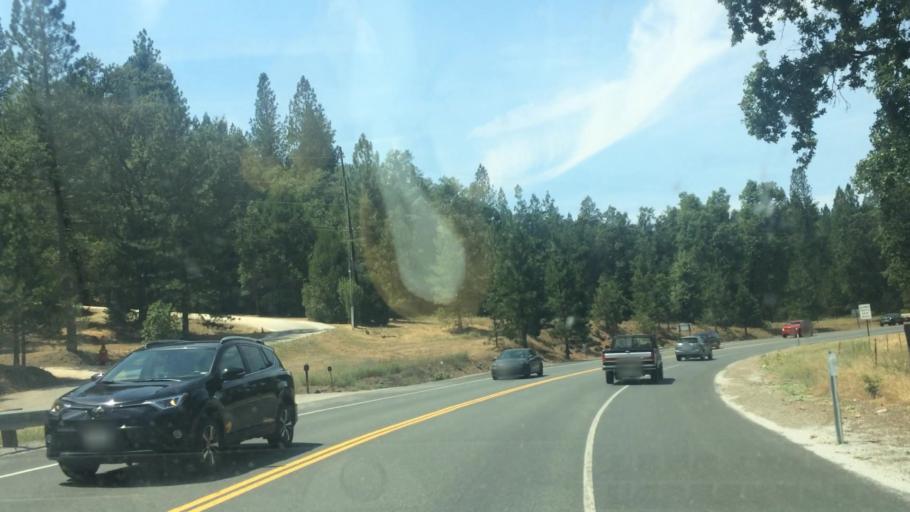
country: US
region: California
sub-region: Amador County
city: Pine Grove
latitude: 38.3993
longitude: -120.6335
